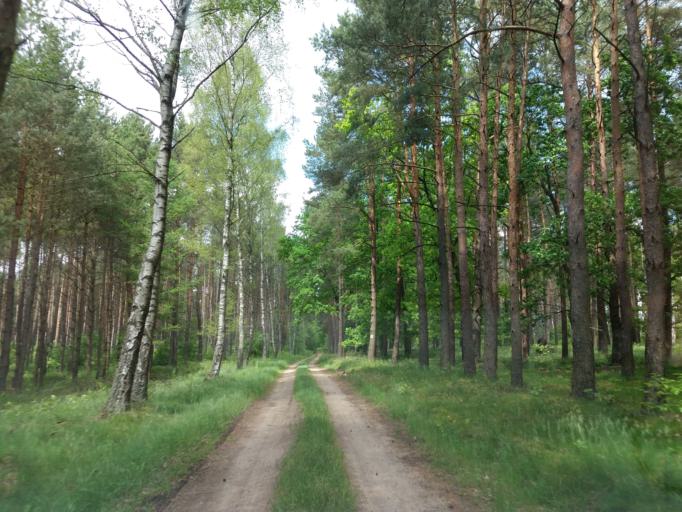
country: PL
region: West Pomeranian Voivodeship
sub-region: Powiat choszczenski
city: Drawno
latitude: 53.2630
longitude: 15.7454
